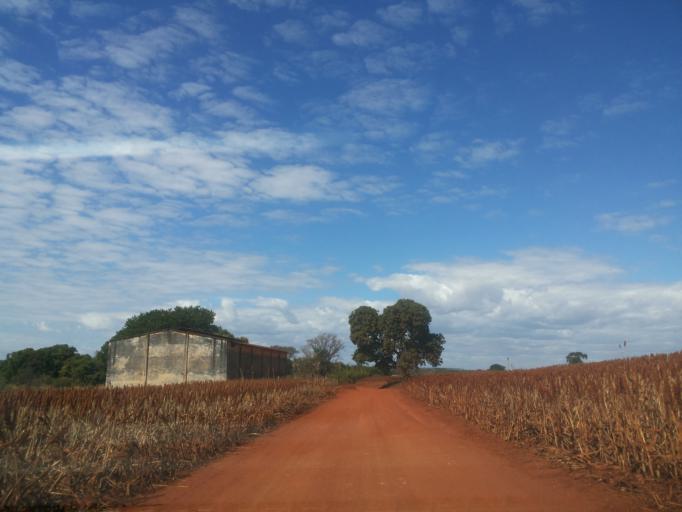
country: BR
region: Minas Gerais
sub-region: Centralina
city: Centralina
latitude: -18.5570
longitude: -49.2348
